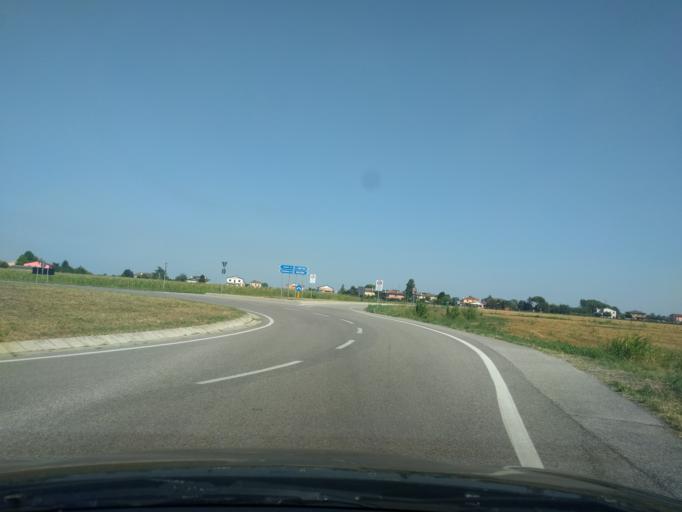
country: IT
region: Veneto
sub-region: Provincia di Rovigo
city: Mardimago
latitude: 45.0920
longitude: 11.8275
